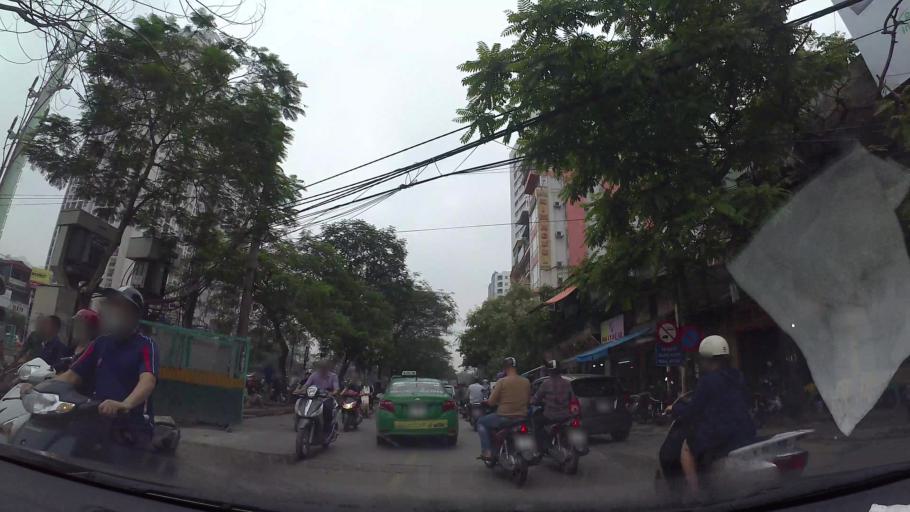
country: VN
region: Ha Noi
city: Hai BaTrung
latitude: 20.9960
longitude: 105.8620
